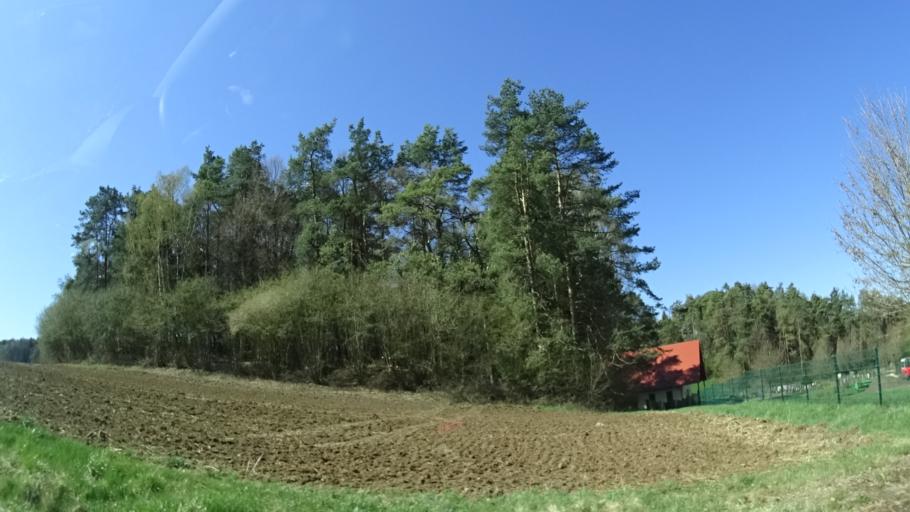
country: DE
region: Bavaria
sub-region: Regierungsbezirk Mittelfranken
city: Alfeld
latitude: 49.4234
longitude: 11.5516
